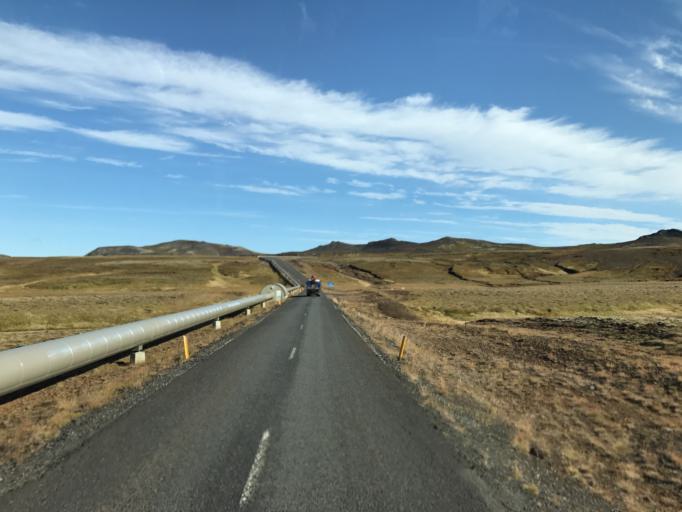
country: IS
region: South
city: Hveragerdi
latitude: 64.1224
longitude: -21.3437
